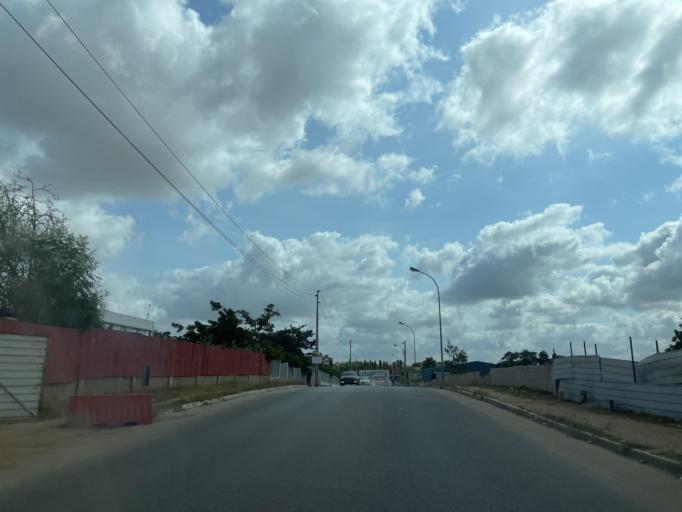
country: AO
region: Luanda
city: Luanda
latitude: -8.9208
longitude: 13.2030
